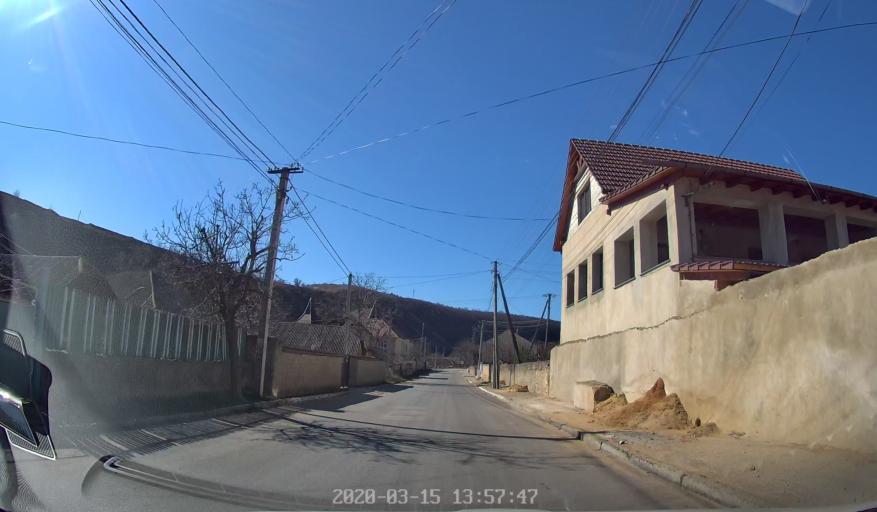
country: MD
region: Telenesti
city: Cocieri
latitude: 47.3110
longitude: 28.9774
